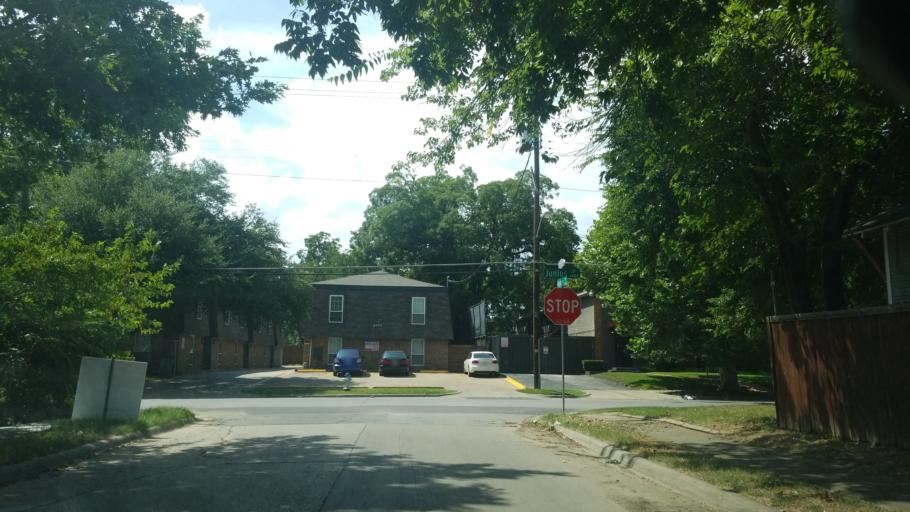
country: US
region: Texas
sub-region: Dallas County
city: Dallas
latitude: 32.7980
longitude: -96.7694
